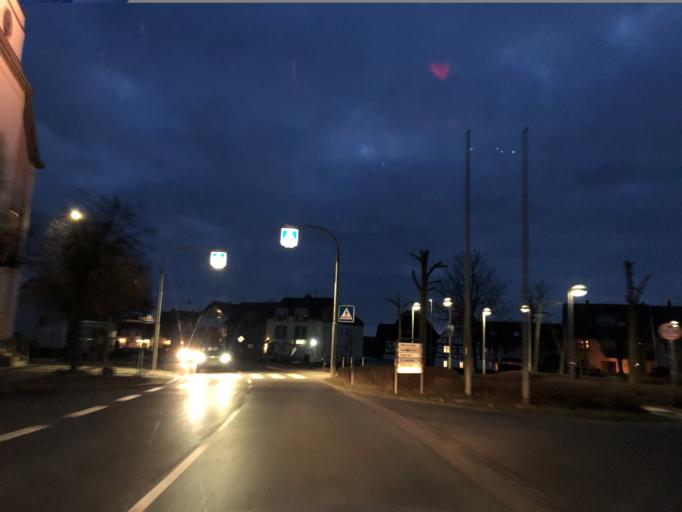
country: DE
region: Rheinland-Pfalz
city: Singhofen
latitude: 50.2744
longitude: 7.8363
